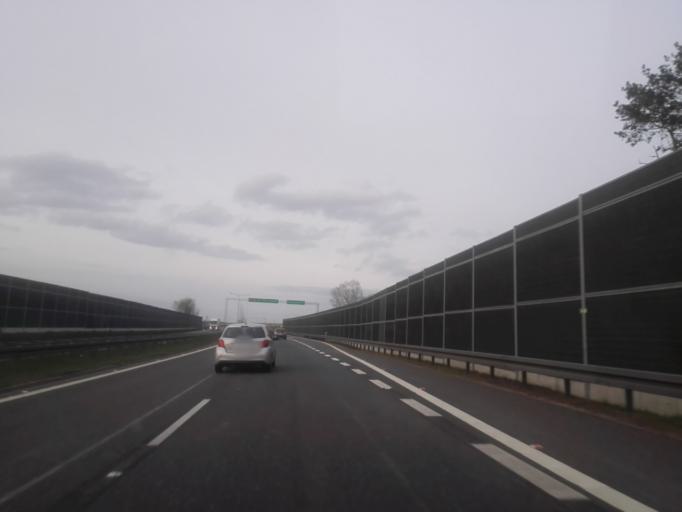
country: PL
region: Masovian Voivodeship
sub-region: Powiat zyrardowski
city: Mszczonow
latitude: 51.9325
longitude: 20.4738
